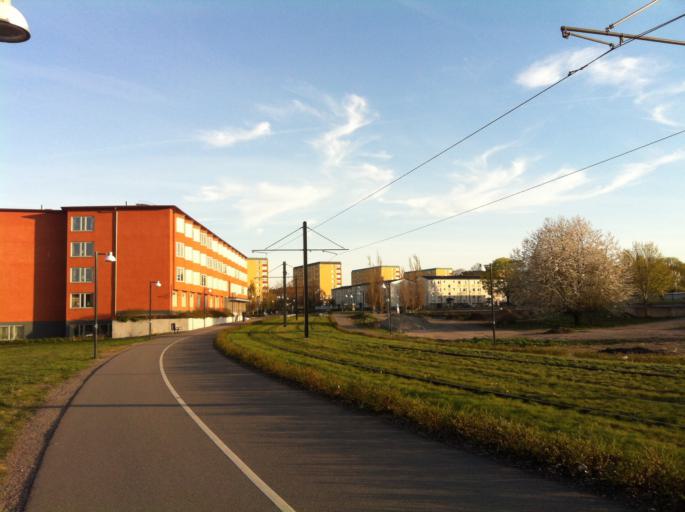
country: SE
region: OEstergoetland
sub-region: Norrkopings Kommun
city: Norrkoping
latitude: 58.5767
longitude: 16.2024
